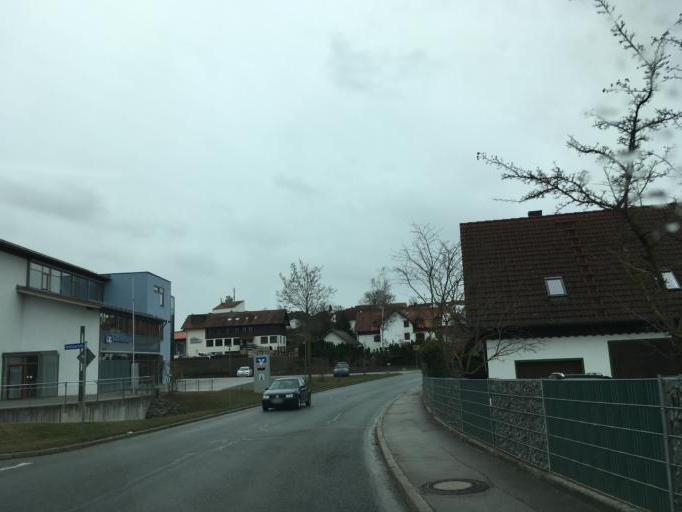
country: DE
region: Bavaria
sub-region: Upper Bavaria
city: Rudelzhausen
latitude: 48.5886
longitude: 11.7675
